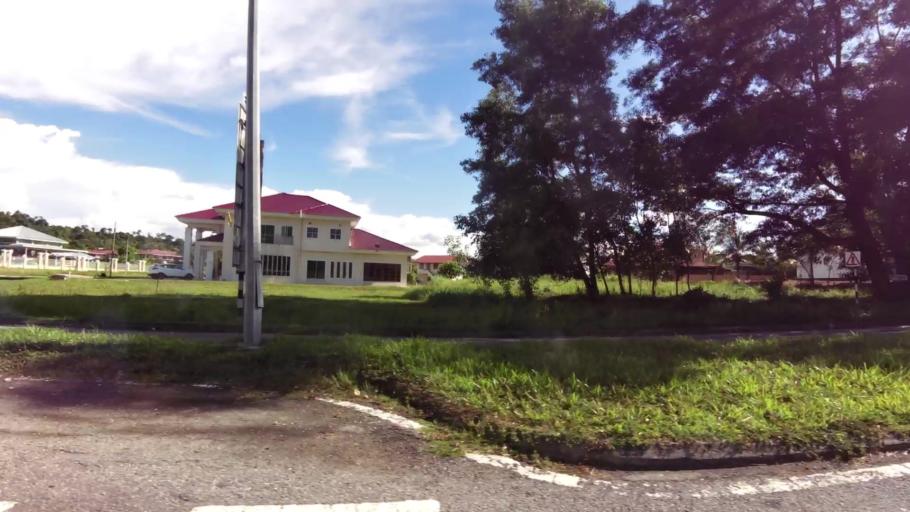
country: BN
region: Brunei and Muara
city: Bandar Seri Begawan
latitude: 4.9807
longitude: 114.9595
